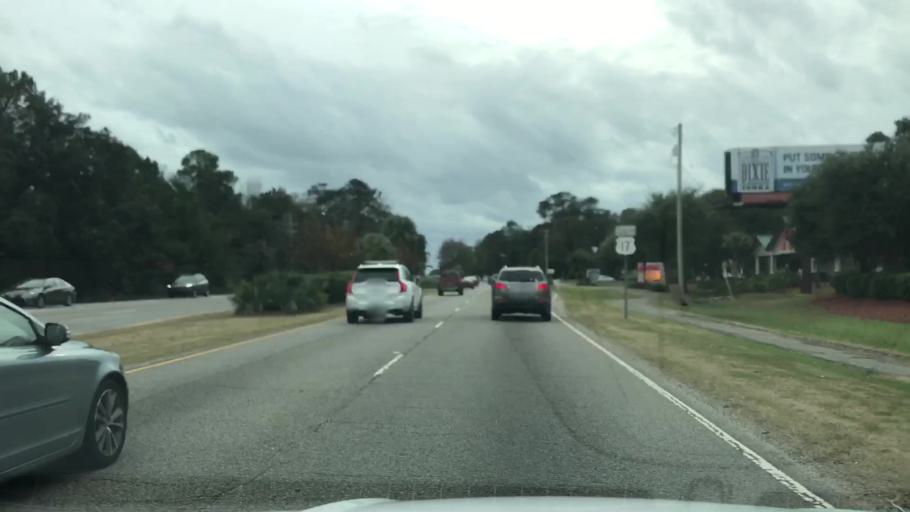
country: US
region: South Carolina
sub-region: Georgetown County
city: Murrells Inlet
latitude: 33.4802
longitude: -79.0992
